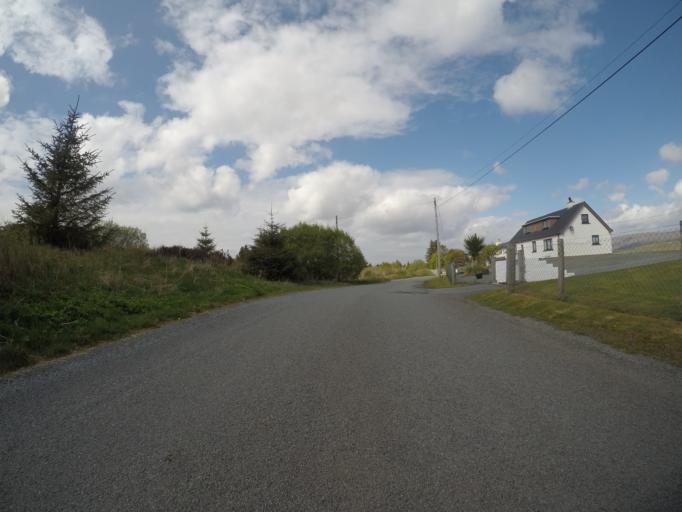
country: GB
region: Scotland
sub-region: Highland
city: Isle of Skye
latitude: 57.4647
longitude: -6.3332
